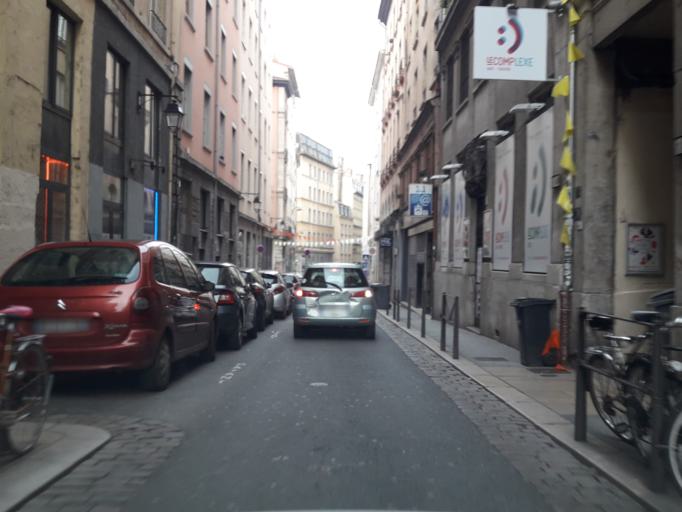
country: FR
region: Rhone-Alpes
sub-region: Departement du Rhone
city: Caluire-et-Cuire
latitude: 45.7692
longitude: 4.8331
